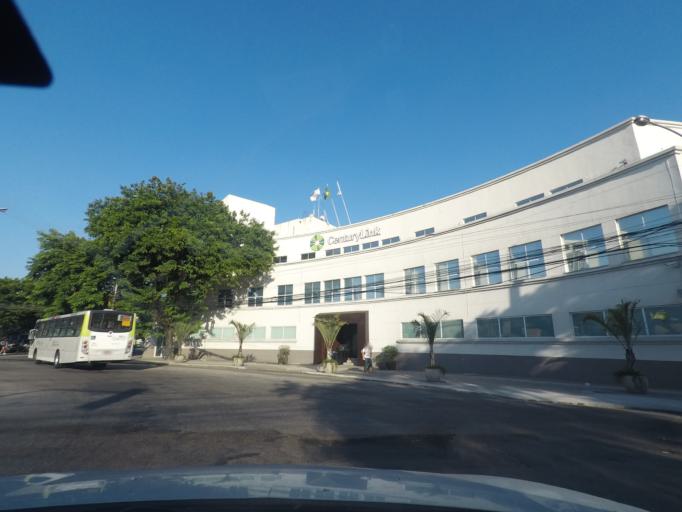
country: BR
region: Rio de Janeiro
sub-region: Rio De Janeiro
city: Rio de Janeiro
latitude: -22.9050
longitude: -43.2182
